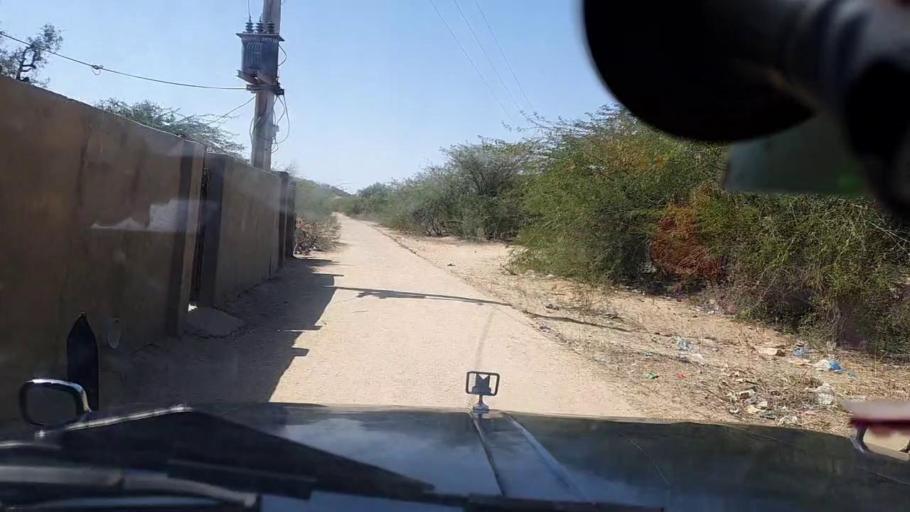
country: PK
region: Sindh
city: Mithi
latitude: 24.5949
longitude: 69.7081
